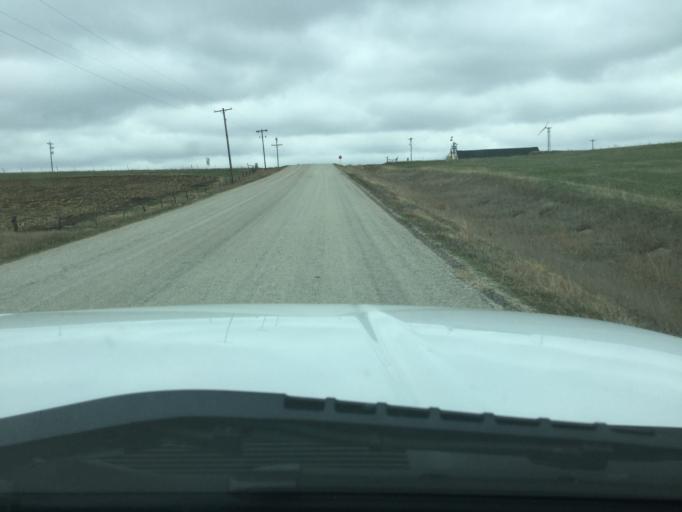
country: US
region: Kansas
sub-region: Nemaha County
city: Seneca
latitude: 39.7400
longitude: -96.0310
